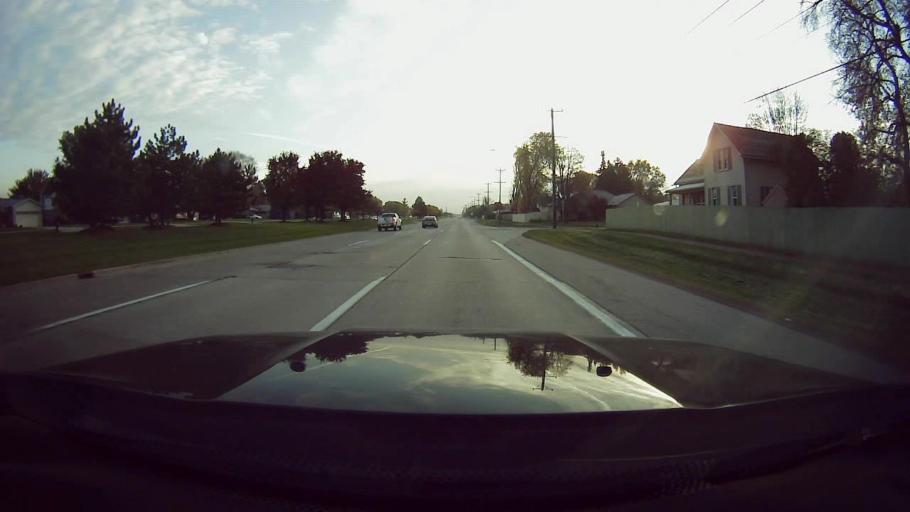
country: US
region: Michigan
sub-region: Macomb County
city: Sterling Heights
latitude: 42.5659
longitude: -83.0226
